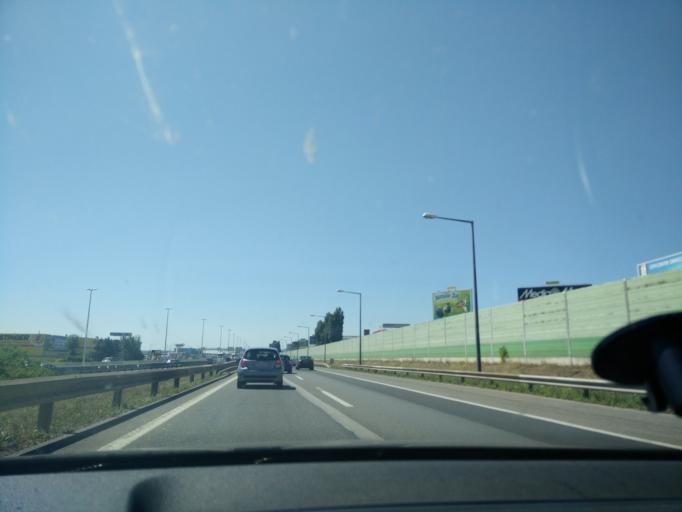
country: AT
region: Lower Austria
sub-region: Politischer Bezirk Modling
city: Vosendorf
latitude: 48.1436
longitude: 16.3341
